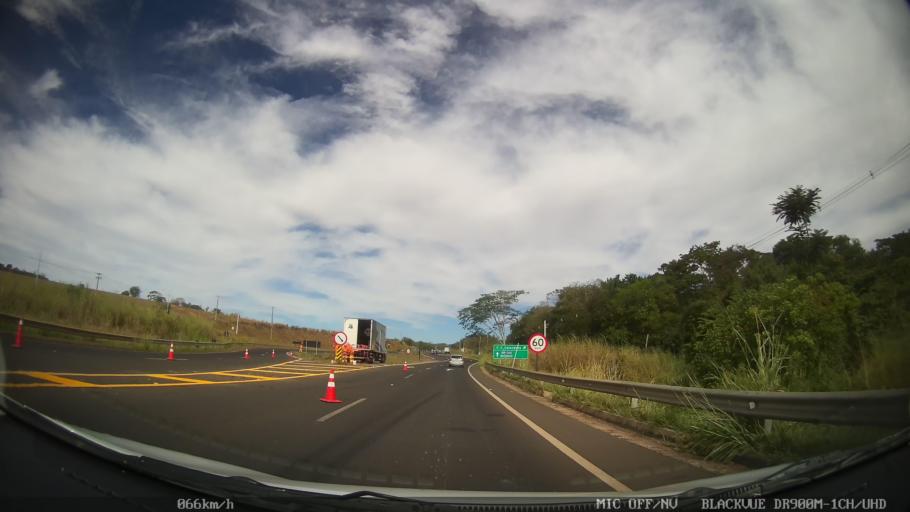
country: BR
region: Sao Paulo
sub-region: Catanduva
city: Catanduva
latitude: -21.1634
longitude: -48.9880
